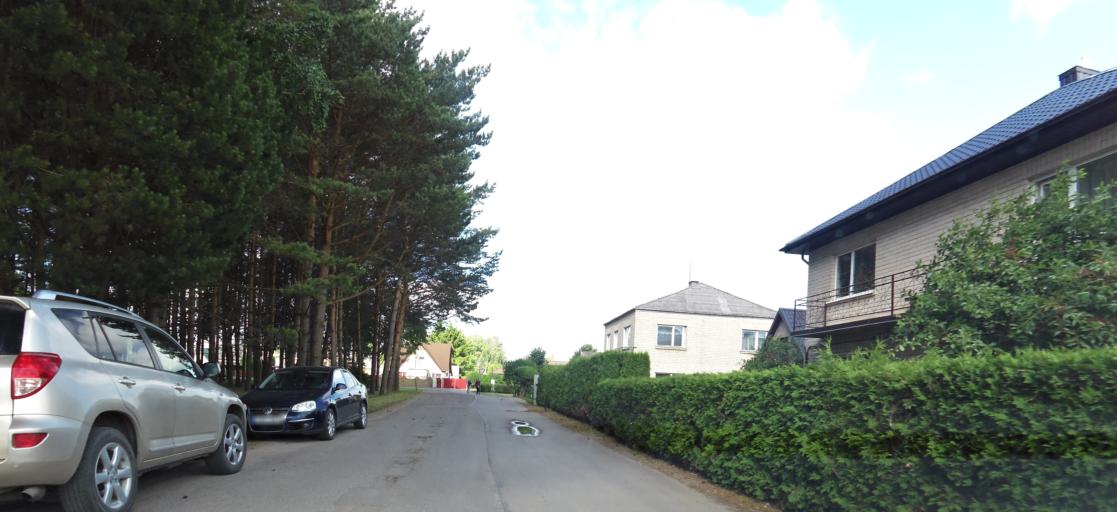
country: LT
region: Panevezys
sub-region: Birzai
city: Birzai
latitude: 56.1897
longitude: 24.7577
